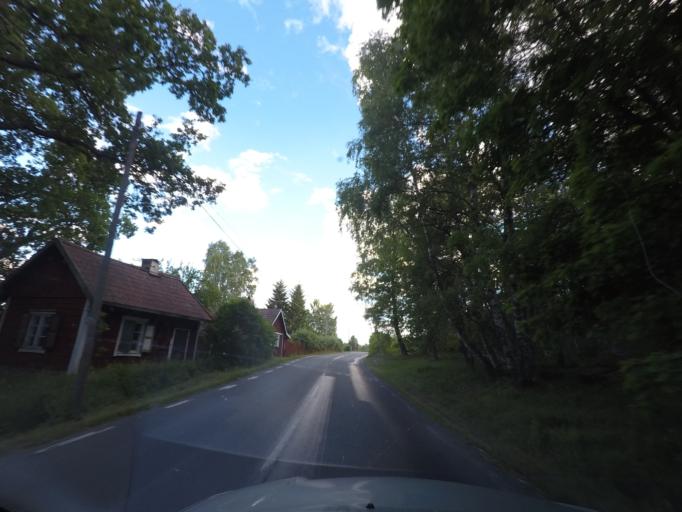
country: SE
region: Stockholm
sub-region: Sigtuna Kommun
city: Marsta
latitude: 59.6958
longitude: 17.9744
